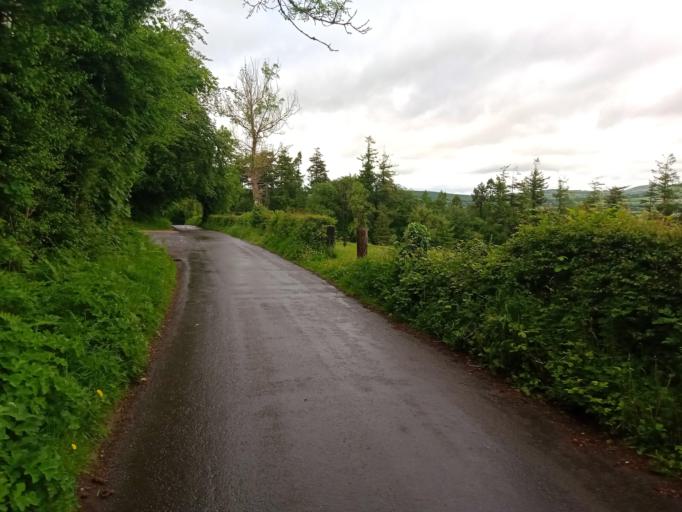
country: IE
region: Leinster
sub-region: Kilkenny
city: Thomastown
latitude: 52.4800
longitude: -7.0641
